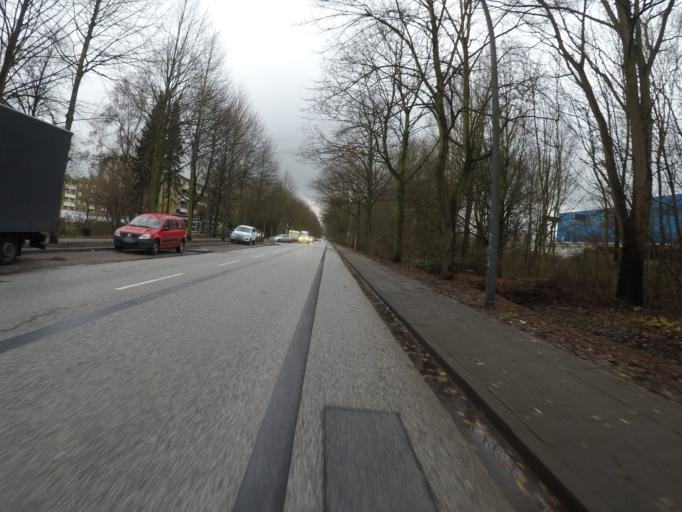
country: DE
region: Hamburg
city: Harburg
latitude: 53.4926
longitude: 9.9904
